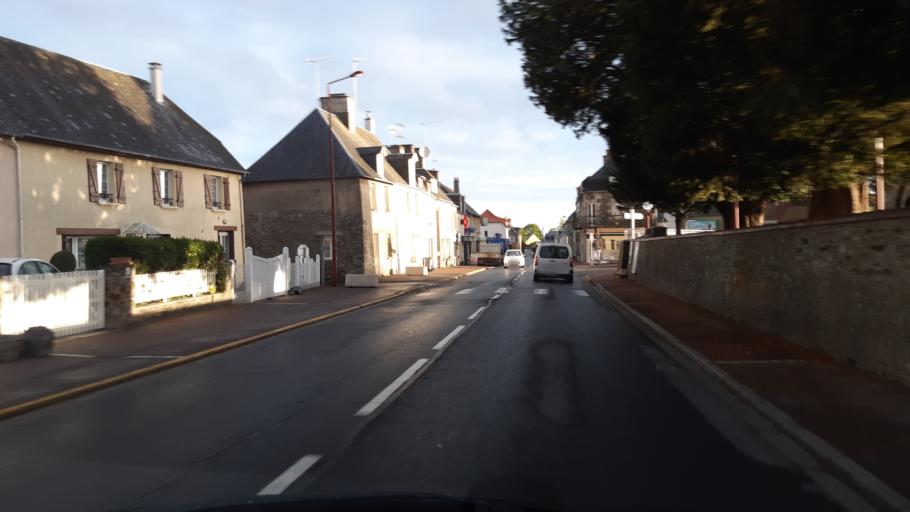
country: FR
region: Lower Normandy
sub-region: Departement de la Manche
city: Agneaux
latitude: 49.0485
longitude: -1.1284
